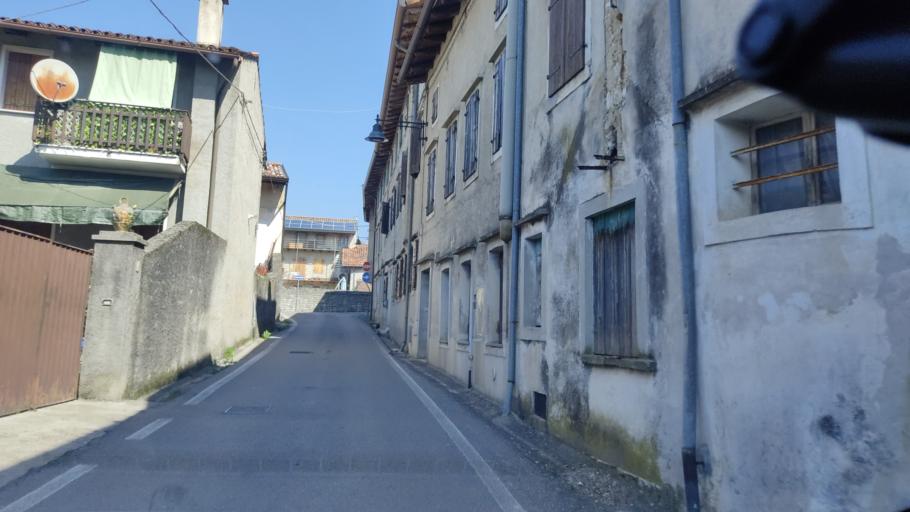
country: IT
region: Friuli Venezia Giulia
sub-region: Provincia di Pordenone
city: Budoia
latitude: 46.0329
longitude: 12.5319
